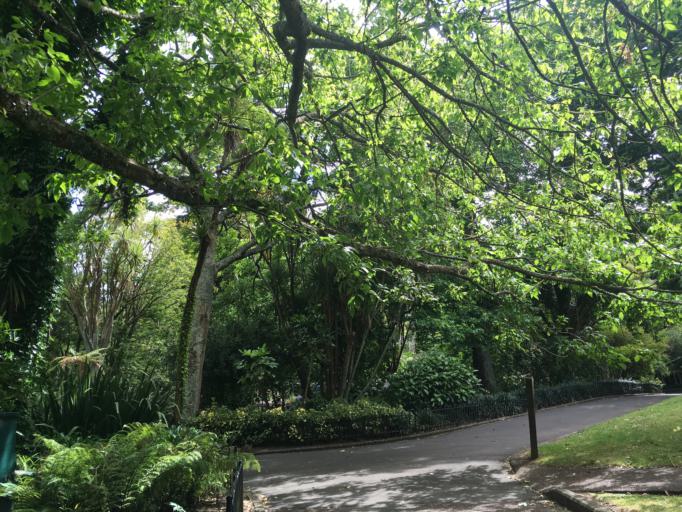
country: NZ
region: Auckland
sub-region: Auckland
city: Auckland
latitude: -36.8596
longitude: 174.7734
